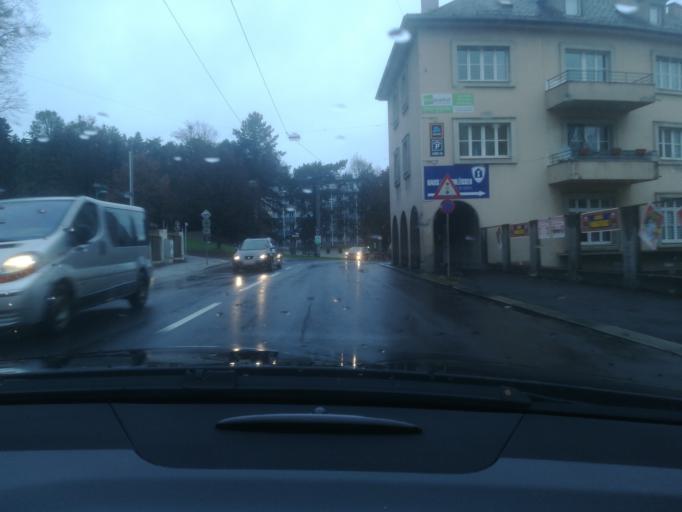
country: AT
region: Upper Austria
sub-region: Linz Stadt
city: Linz
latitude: 48.2945
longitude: 14.2844
